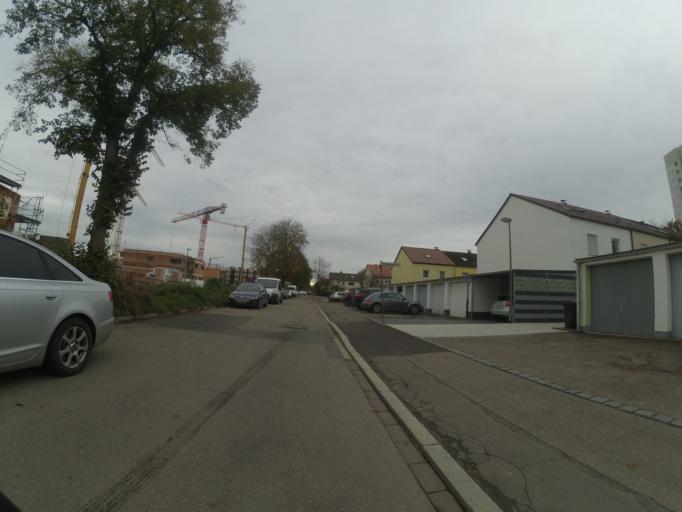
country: DE
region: Bavaria
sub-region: Swabia
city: Neu-Ulm
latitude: 48.3702
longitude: 10.0168
